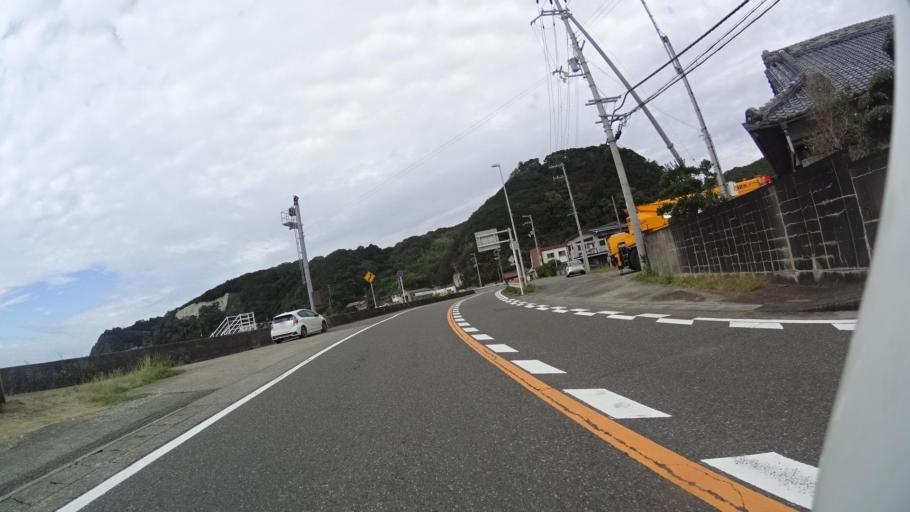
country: JP
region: Wakayama
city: Shingu
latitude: 33.4838
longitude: 135.7607
